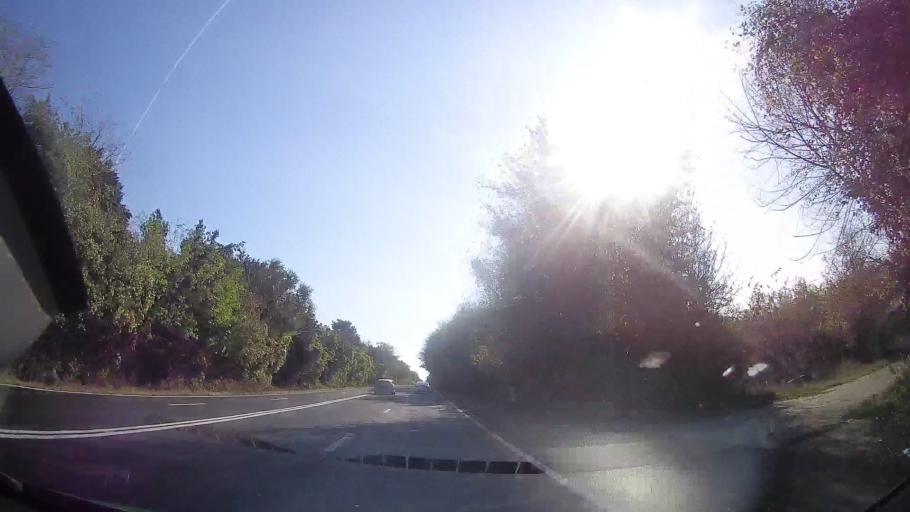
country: RO
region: Constanta
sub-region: Comuna Douazeci si Trei August
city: Dulcesti
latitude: 43.8713
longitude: 28.5744
